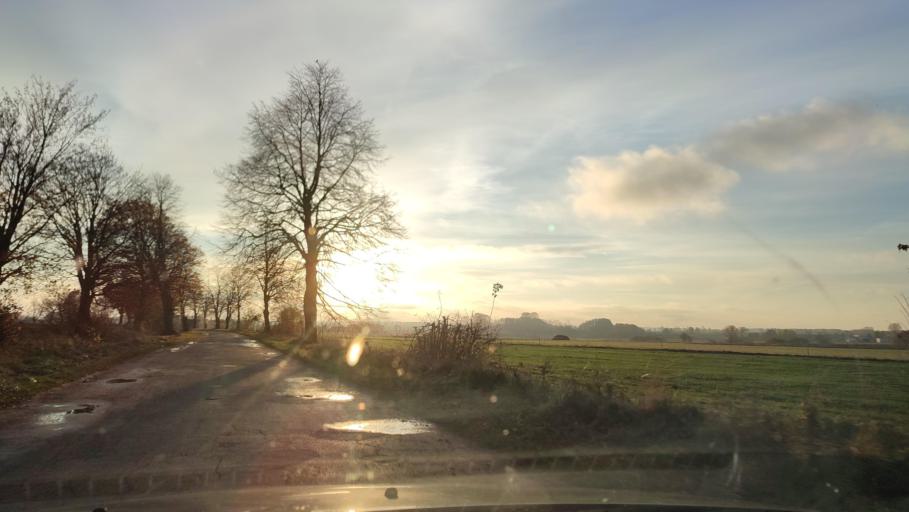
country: PL
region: Masovian Voivodeship
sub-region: Powiat mlawski
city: Wieczfnia Koscielna
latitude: 53.2497
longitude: 20.5845
